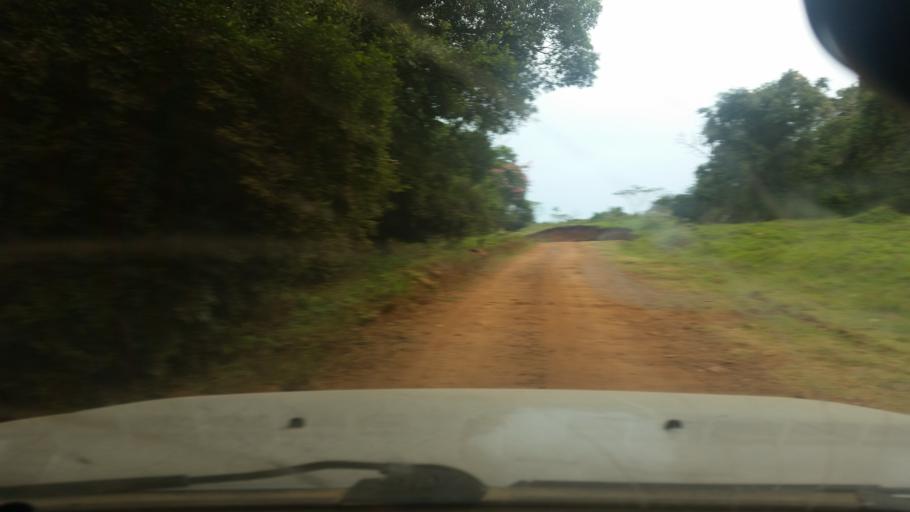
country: PY
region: Guaira
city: Independencia
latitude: -25.8090
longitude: -56.2756
